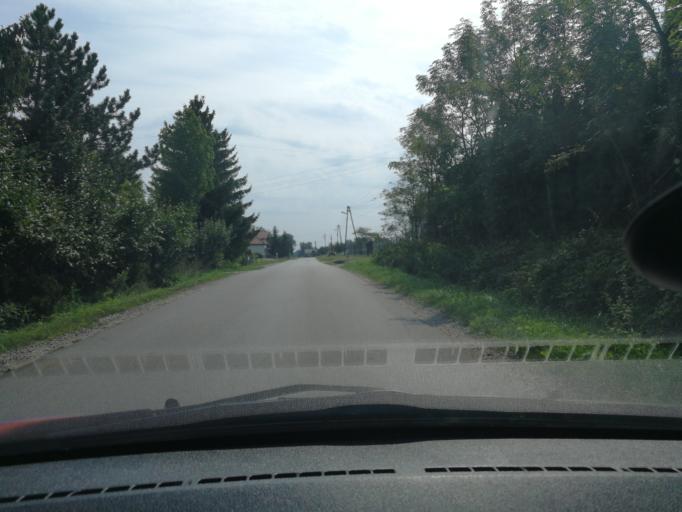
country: PL
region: Lodz Voivodeship
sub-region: Powiat skierniewicki
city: Makow
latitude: 51.9887
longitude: 20.0892
